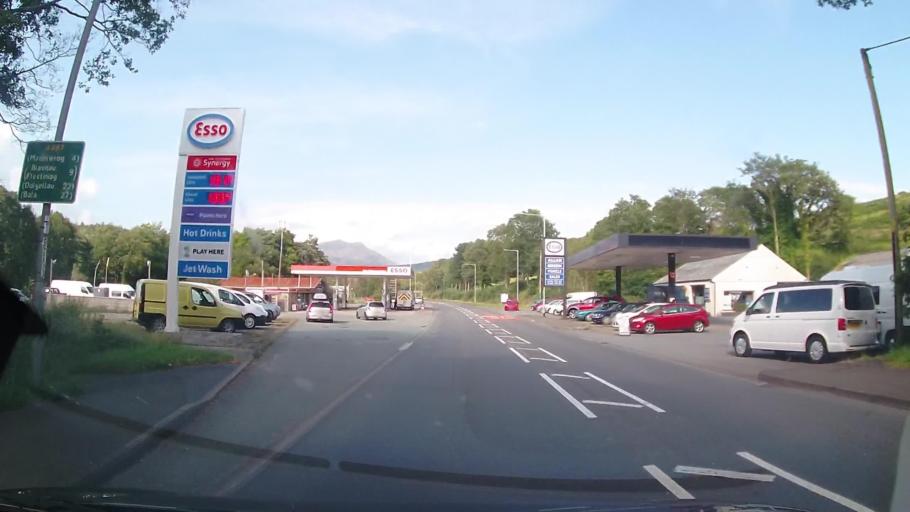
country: GB
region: Wales
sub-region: Gwynedd
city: Penrhyndeudraeth
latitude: 52.9318
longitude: -4.0641
